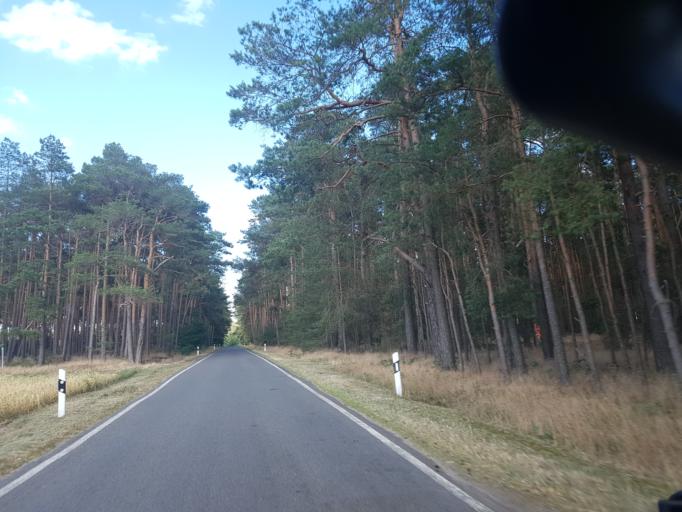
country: DE
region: Brandenburg
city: Herzberg
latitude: 51.7833
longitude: 13.2489
